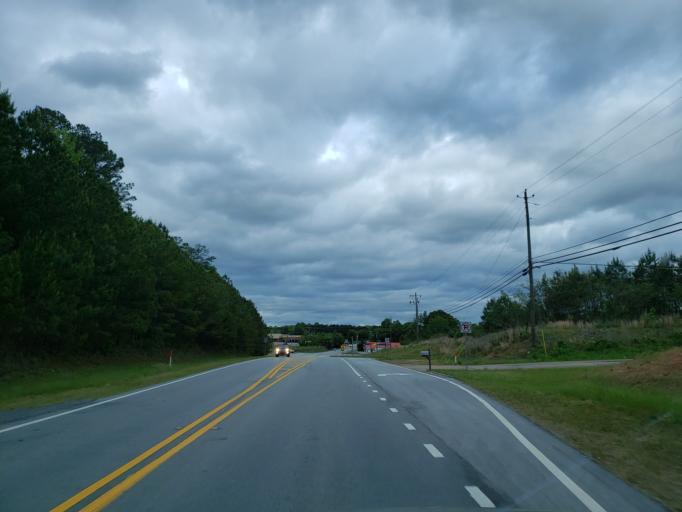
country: US
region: Georgia
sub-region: Paulding County
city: Dallas
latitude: 33.8665
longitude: -84.8448
